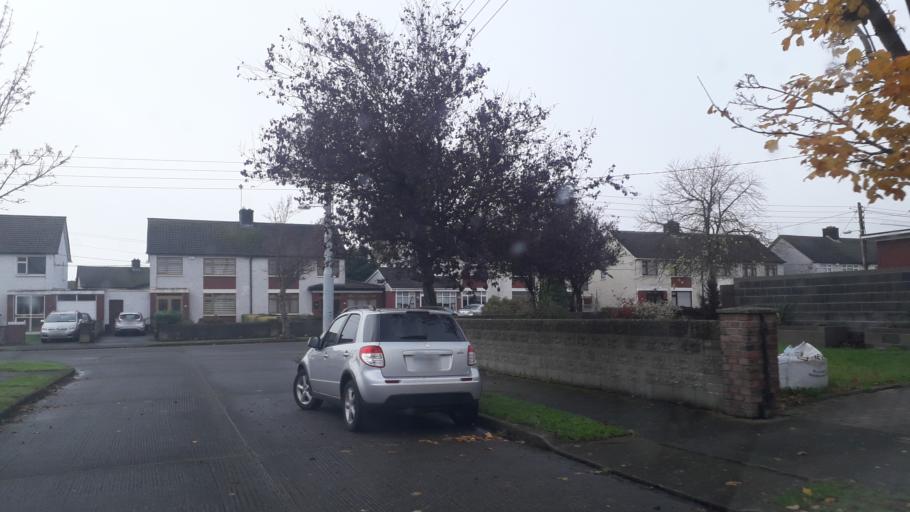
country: IE
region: Leinster
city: Artane
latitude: 53.3914
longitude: -6.2093
